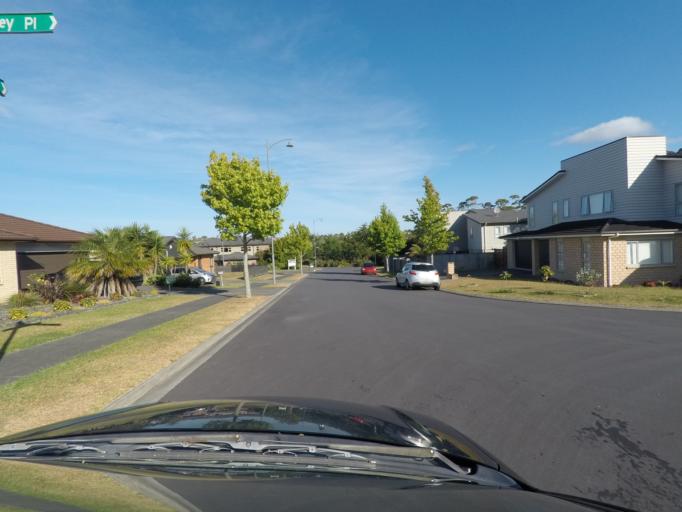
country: NZ
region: Auckland
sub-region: Auckland
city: Waitakere
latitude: -36.8828
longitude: 174.6026
